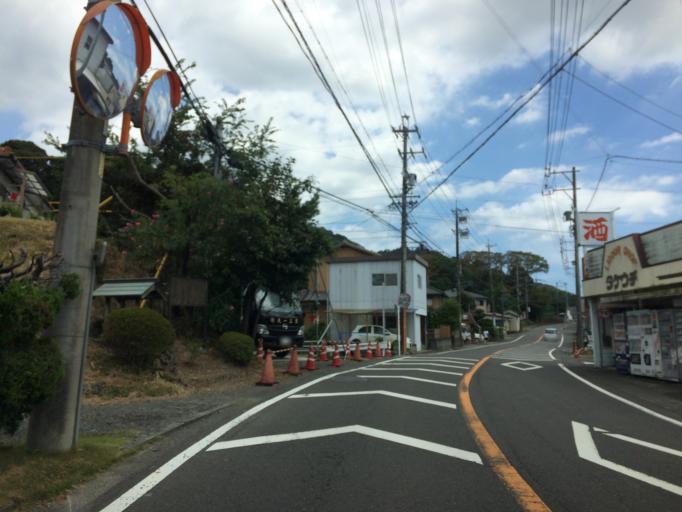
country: JP
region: Shizuoka
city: Yaizu
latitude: 34.9038
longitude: 138.2939
